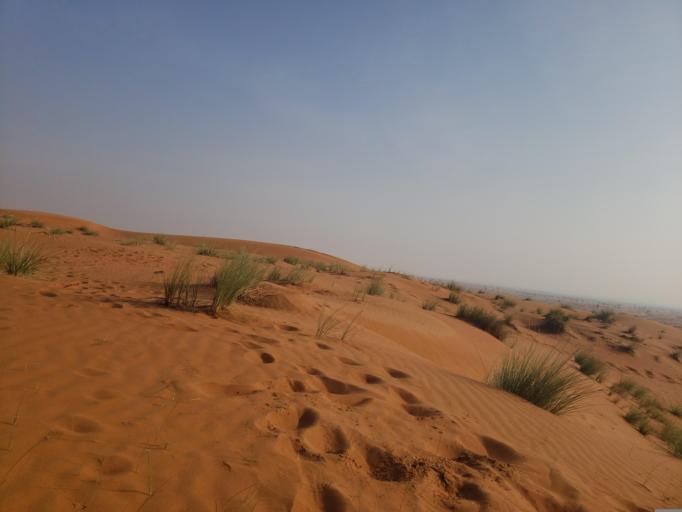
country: AE
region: Ash Shariqah
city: Adh Dhayd
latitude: 25.1381
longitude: 55.8418
